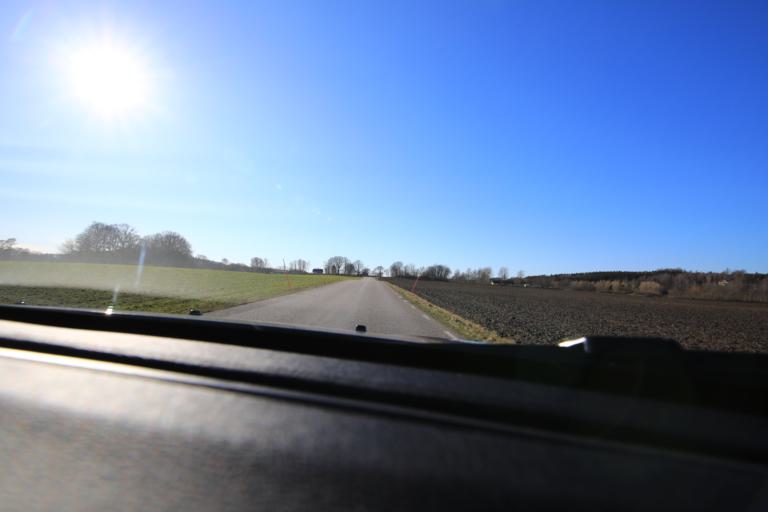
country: SE
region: Halland
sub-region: Varbergs Kommun
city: Tvaaker
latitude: 57.0598
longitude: 12.4456
